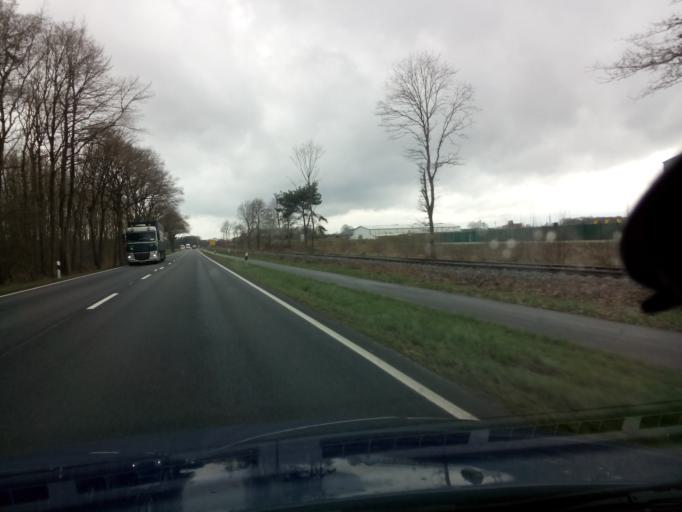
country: DE
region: Lower Saxony
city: Herzlake
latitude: 52.6948
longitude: 7.5658
